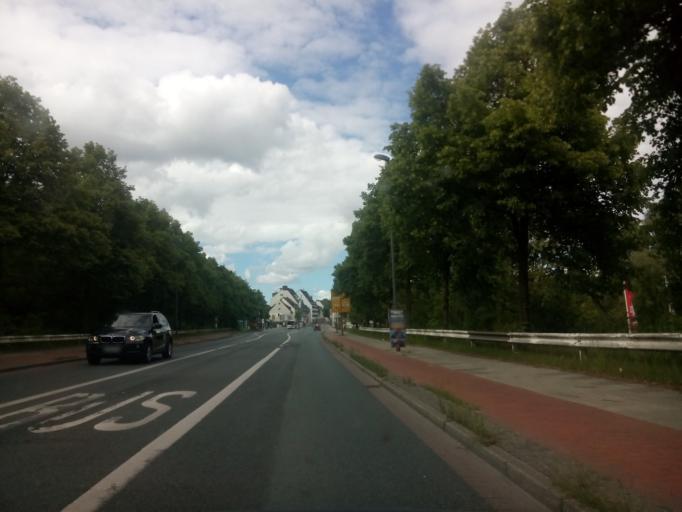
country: DE
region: Lower Saxony
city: Ritterhude
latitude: 53.1656
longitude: 8.7023
